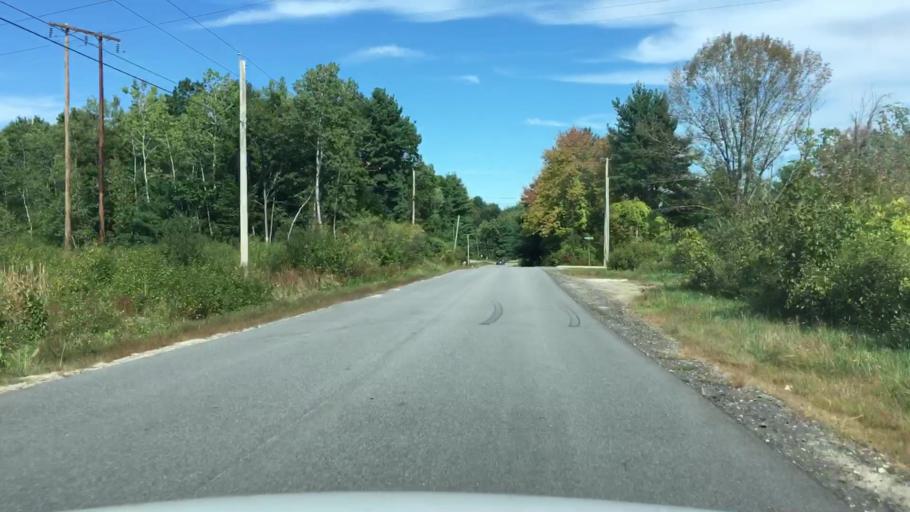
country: US
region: Maine
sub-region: Cumberland County
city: Westbrook
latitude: 43.6715
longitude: -70.3923
